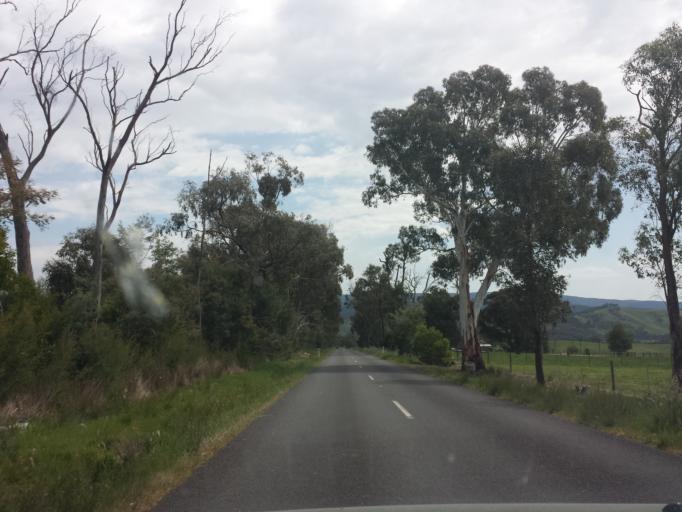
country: AU
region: Victoria
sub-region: Murrindindi
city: Alexandra
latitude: -37.3412
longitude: 145.7286
